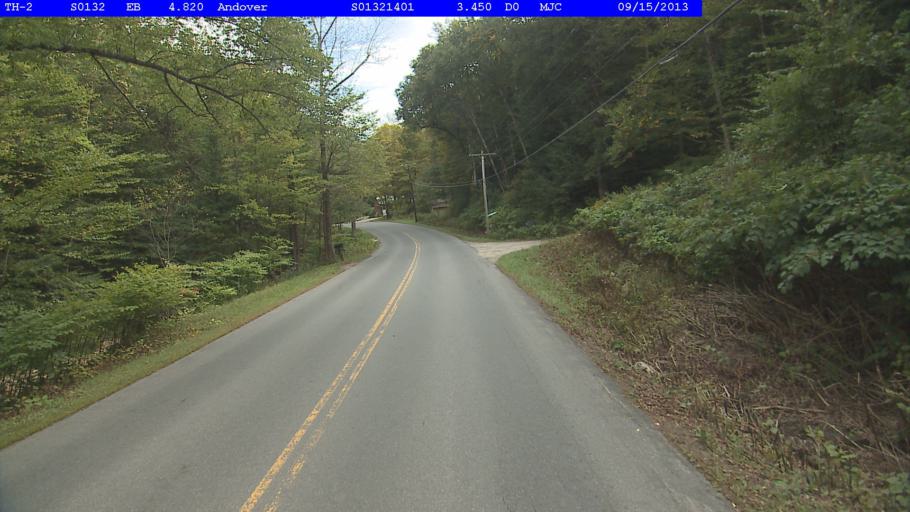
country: US
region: Vermont
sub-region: Windsor County
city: Chester
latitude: 43.2800
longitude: -72.7068
